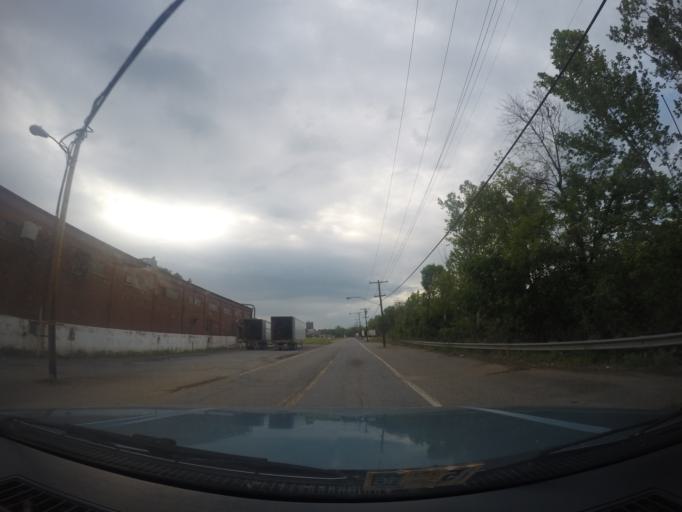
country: US
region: Virginia
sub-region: City of Lynchburg
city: Lynchburg
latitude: 37.4038
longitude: -79.1281
